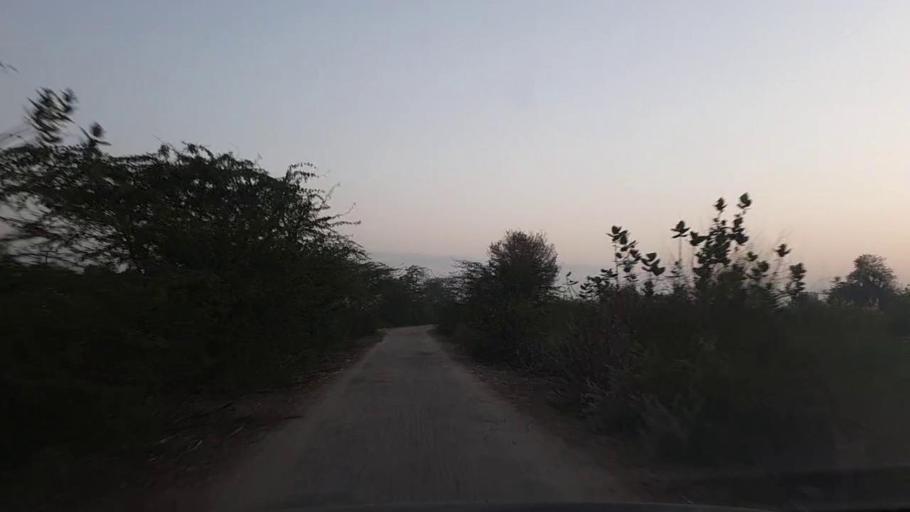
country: PK
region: Sindh
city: Daur
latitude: 26.4842
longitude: 68.4906
